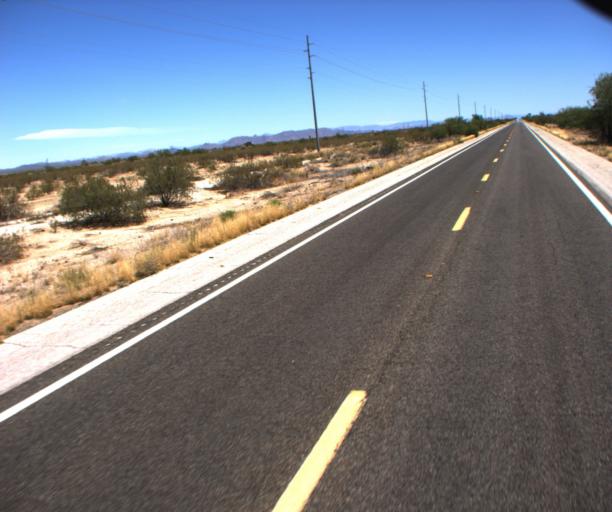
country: US
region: Arizona
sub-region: La Paz County
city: Salome
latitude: 33.8935
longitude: -113.3258
